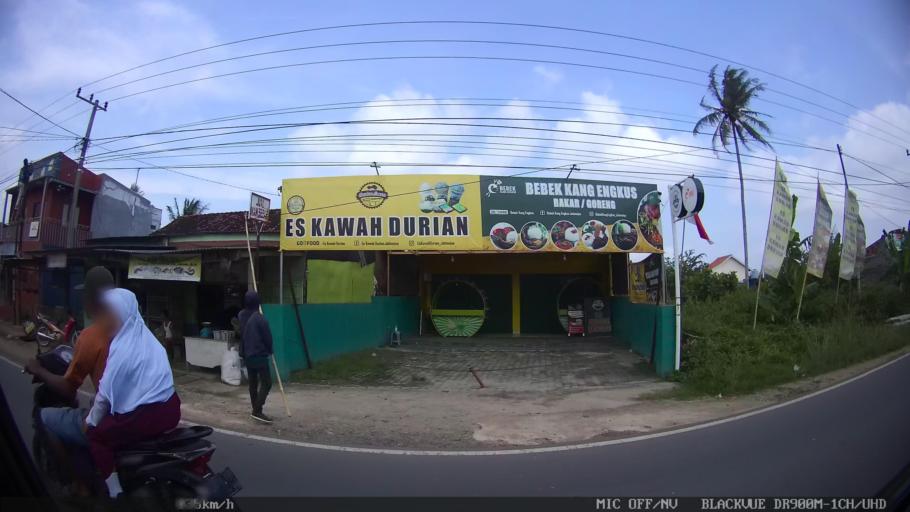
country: ID
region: Lampung
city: Kedaton
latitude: -5.3223
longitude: 105.2894
